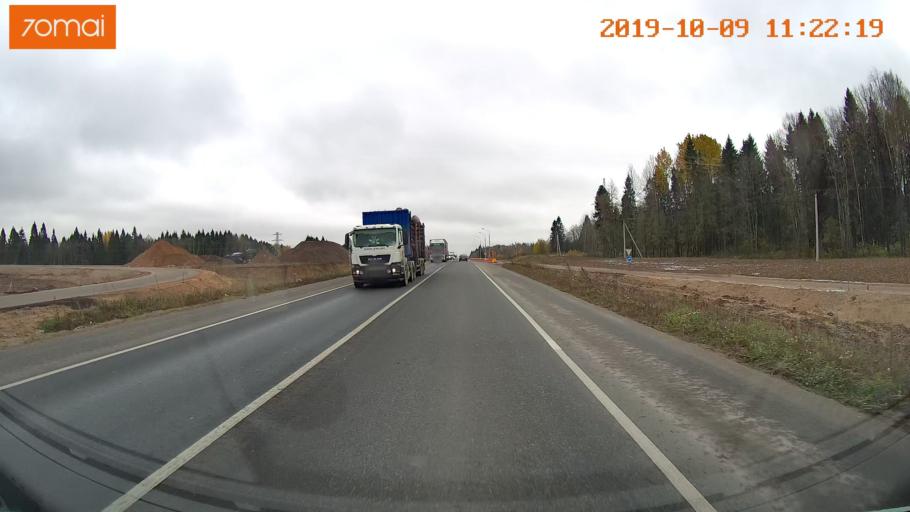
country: RU
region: Vologda
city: Vologda
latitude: 59.1326
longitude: 39.9569
